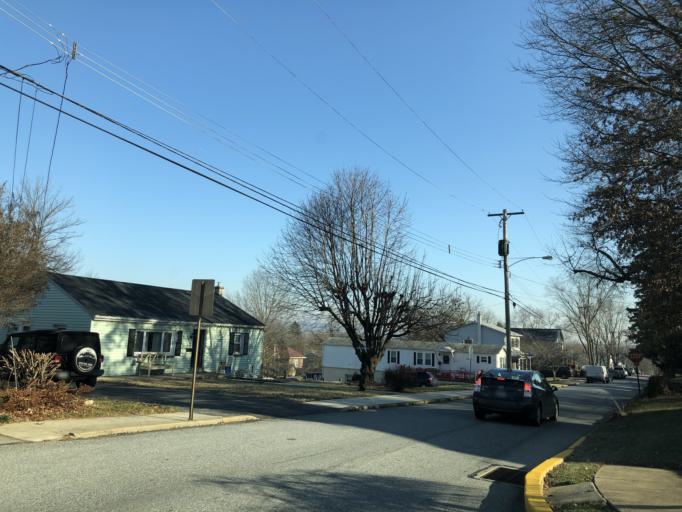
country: US
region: Pennsylvania
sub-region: Chester County
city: Downingtown
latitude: 39.9978
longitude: -75.7144
